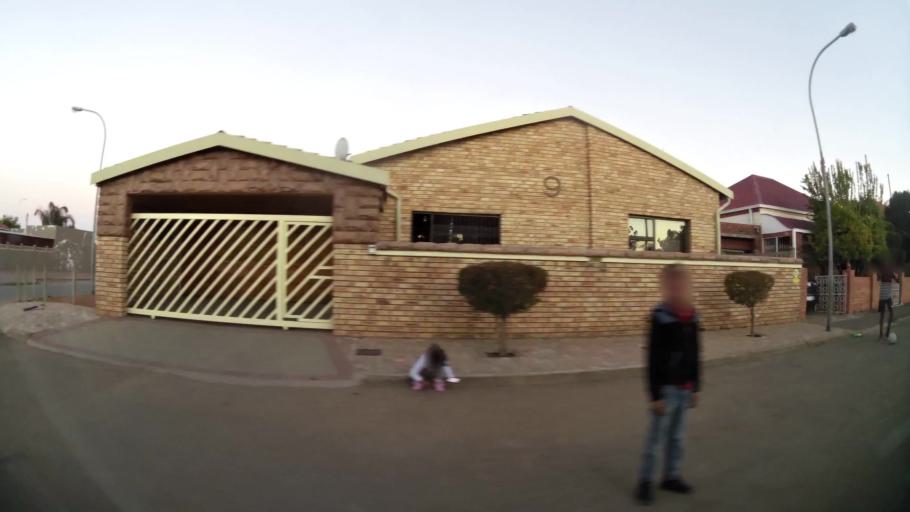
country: ZA
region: Northern Cape
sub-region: Frances Baard District Municipality
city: Kimberley
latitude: -28.7257
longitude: 24.7676
